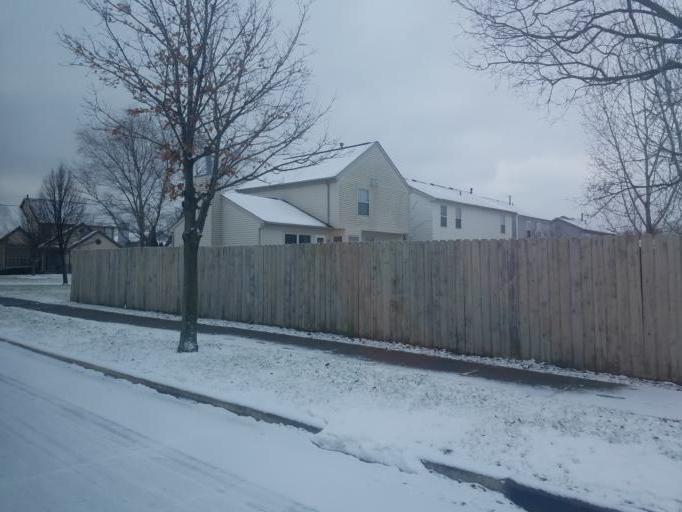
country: US
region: Ohio
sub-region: Franklin County
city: Reynoldsburg
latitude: 39.9958
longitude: -82.7897
